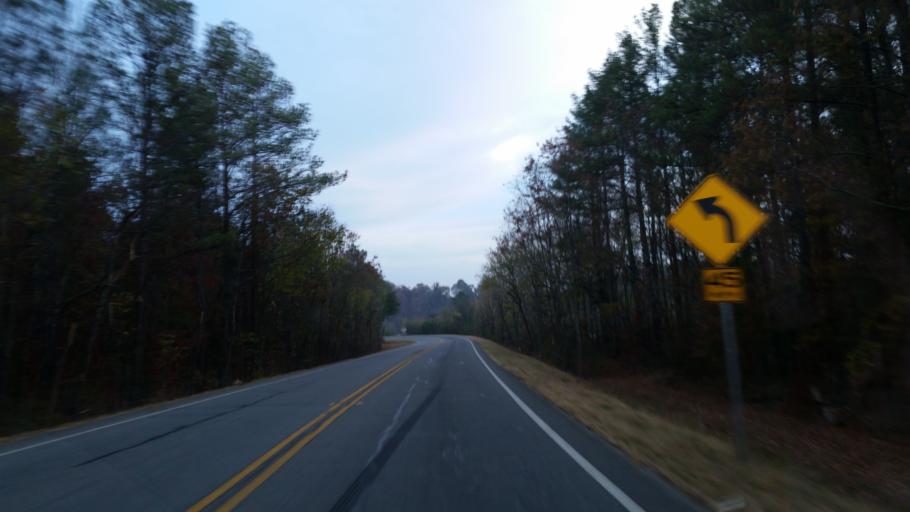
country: US
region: Georgia
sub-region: Murray County
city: Chatsworth
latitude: 34.5943
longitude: -84.7491
